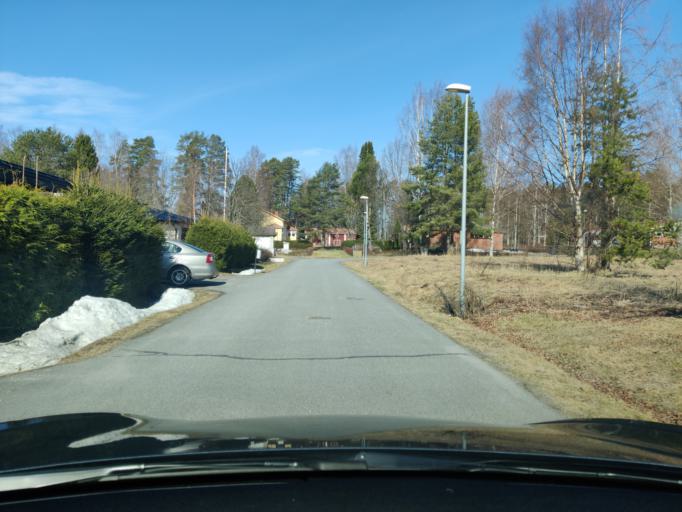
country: FI
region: Northern Savo
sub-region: Kuopio
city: Vehmersalmi
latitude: 62.7650
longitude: 28.0169
